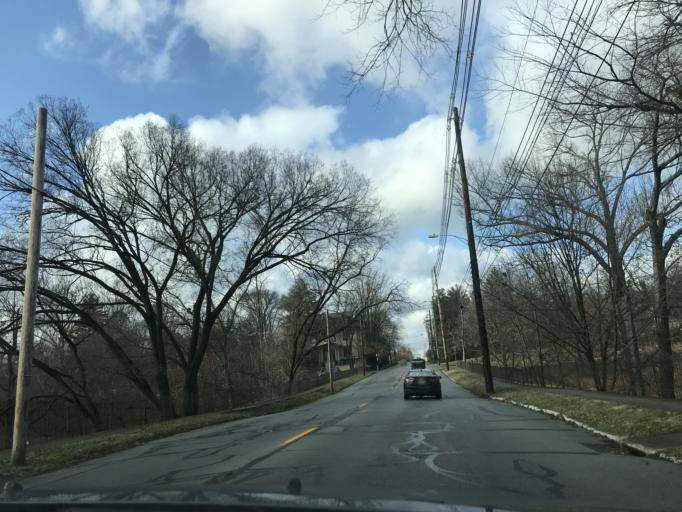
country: US
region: Kentucky
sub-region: Jefferson County
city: Audubon Park
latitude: 38.2310
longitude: -85.7168
